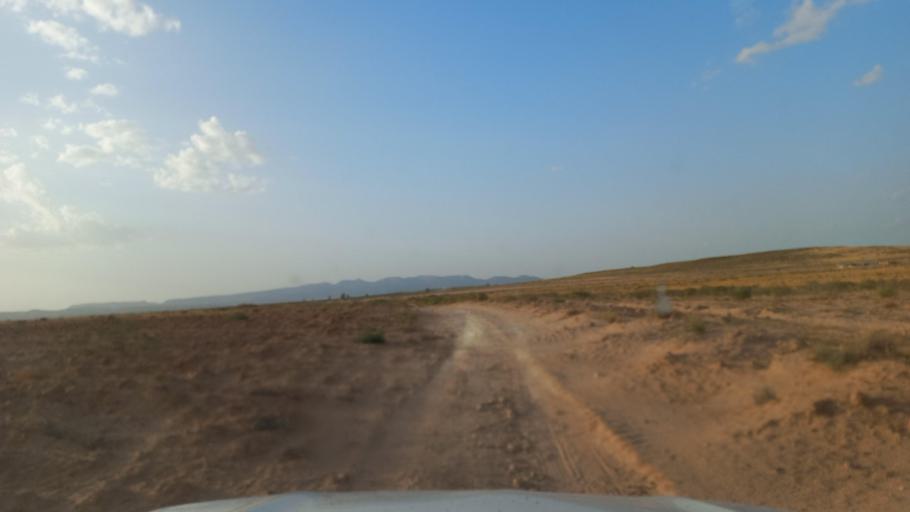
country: TN
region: Al Qasrayn
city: Sbiba
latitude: 35.3060
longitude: 9.0744
